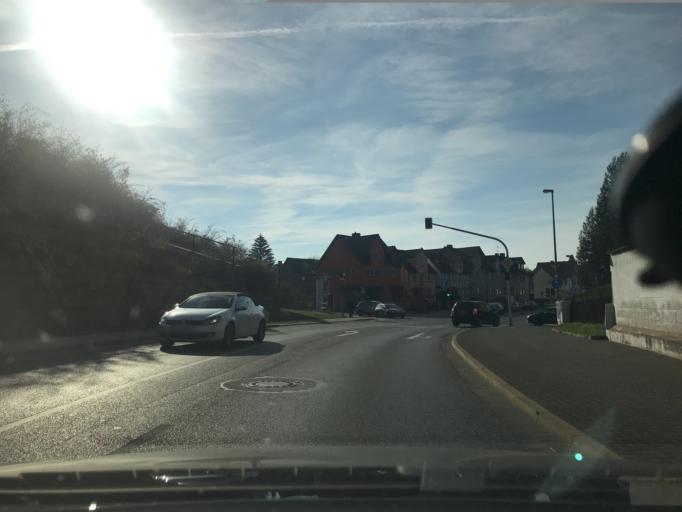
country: DE
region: Hesse
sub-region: Regierungsbezirk Kassel
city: Fuldabruck
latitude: 51.2765
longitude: 9.4537
